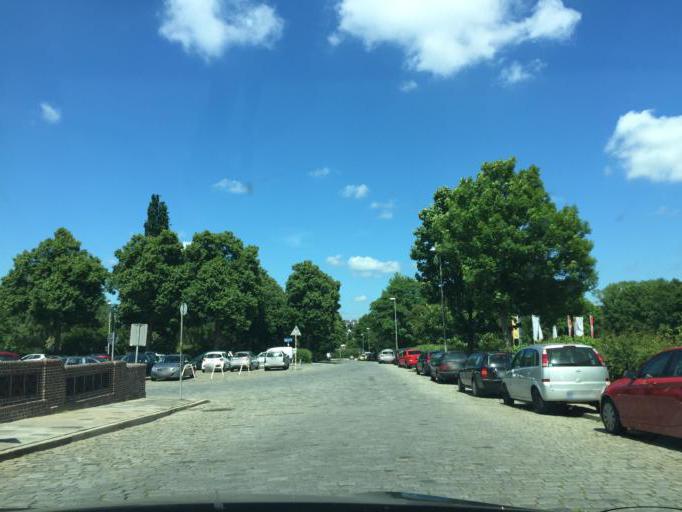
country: DE
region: Schleswig-Holstein
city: Flensburg
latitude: 54.7746
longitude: 9.4375
